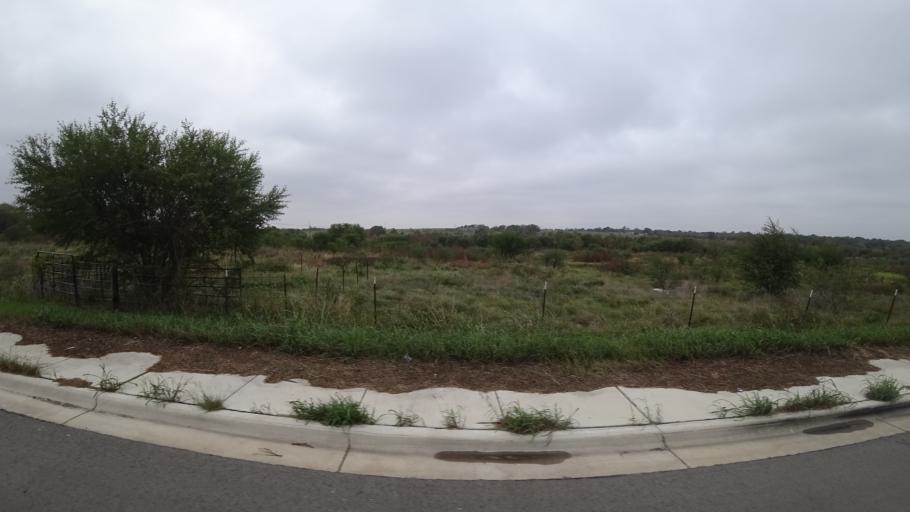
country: US
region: Texas
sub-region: Travis County
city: Pflugerville
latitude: 30.4191
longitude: -97.6148
